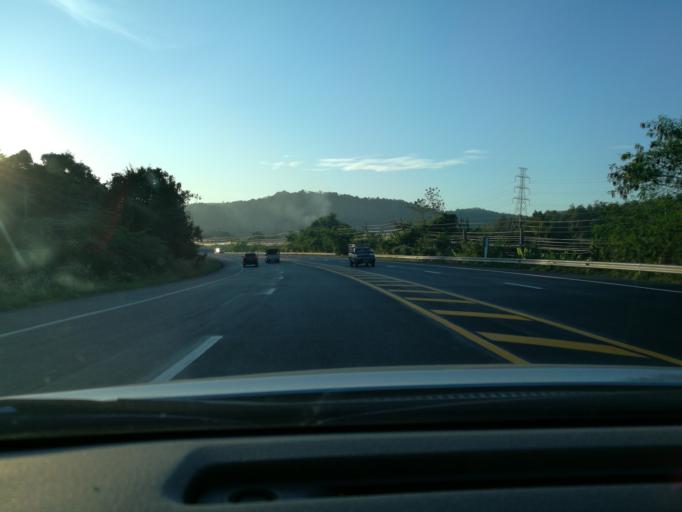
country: TH
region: Phitsanulok
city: Wang Thong
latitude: 16.8663
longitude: 100.4921
